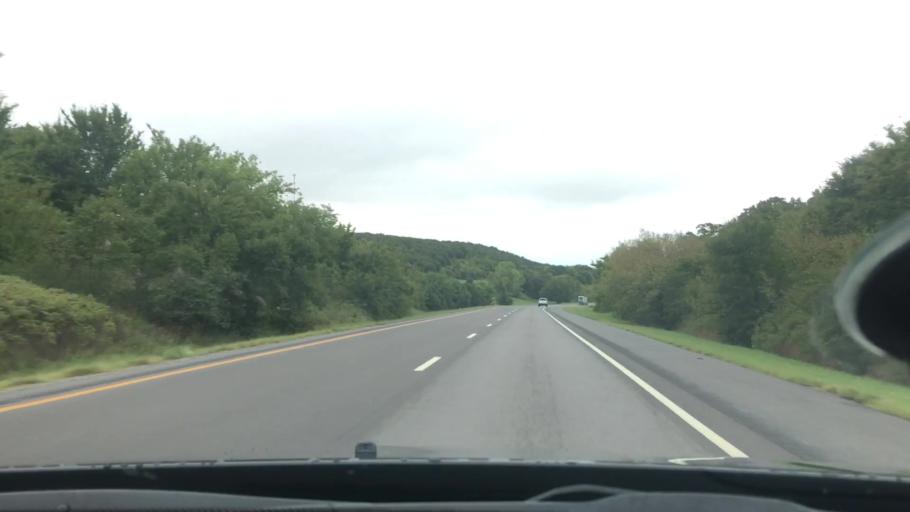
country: US
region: Oklahoma
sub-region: Okmulgee County
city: Morris
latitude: 35.4392
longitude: -95.7852
